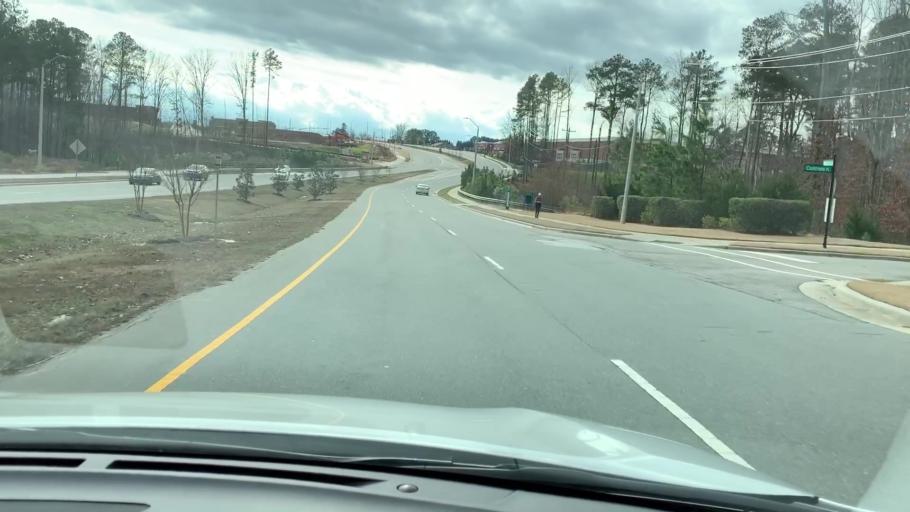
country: US
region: North Carolina
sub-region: Wake County
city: Green Level
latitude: 35.8276
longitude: -78.9013
